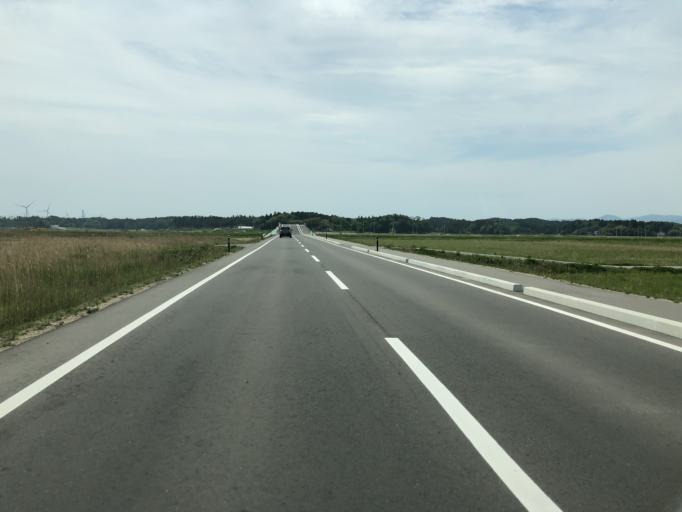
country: JP
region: Fukushima
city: Namie
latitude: 37.7250
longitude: 141.0036
